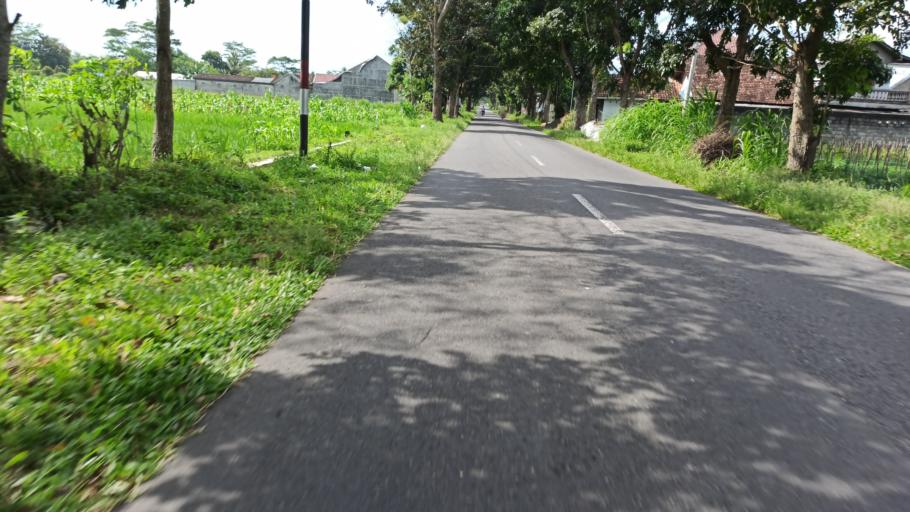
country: ID
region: Daerah Istimewa Yogyakarta
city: Sleman
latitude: -7.6918
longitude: 110.2948
